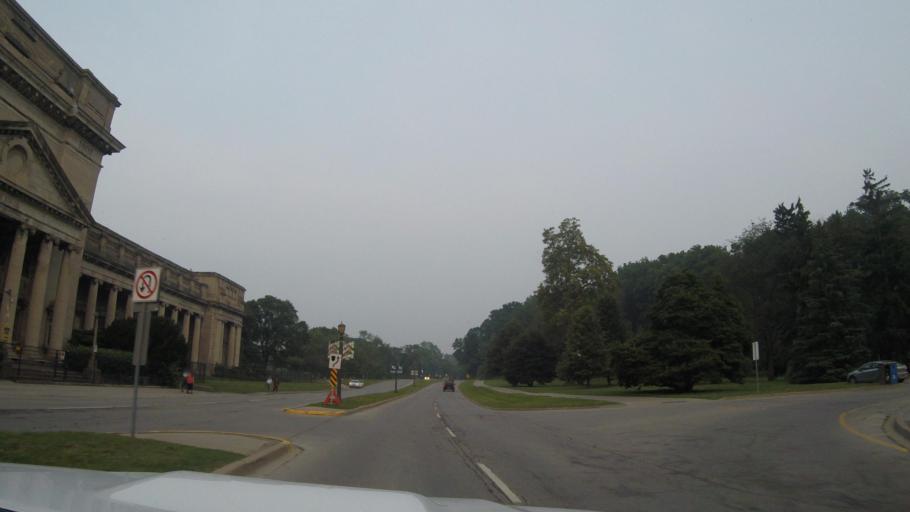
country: US
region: New York
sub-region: Niagara County
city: Niagara Falls
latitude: 43.0719
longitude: -79.0745
